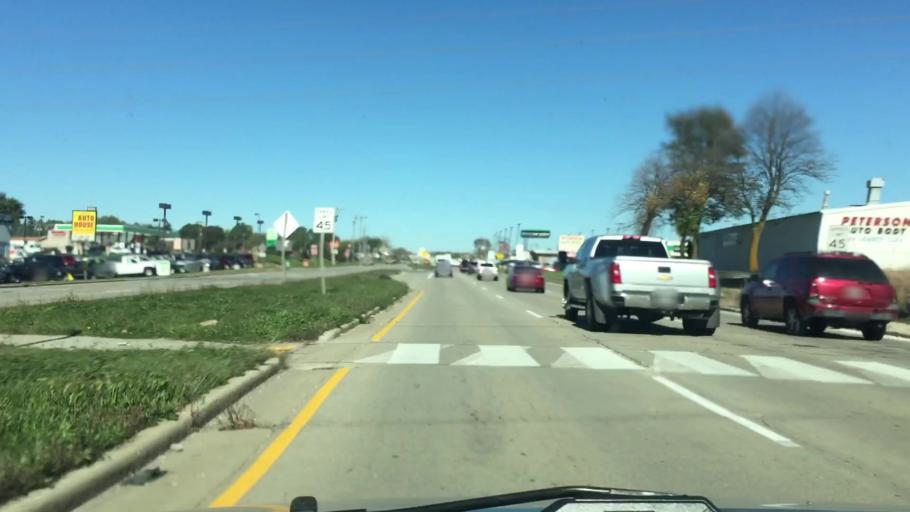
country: US
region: Wisconsin
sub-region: Waukesha County
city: Waukesha
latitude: 43.0101
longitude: -88.2000
